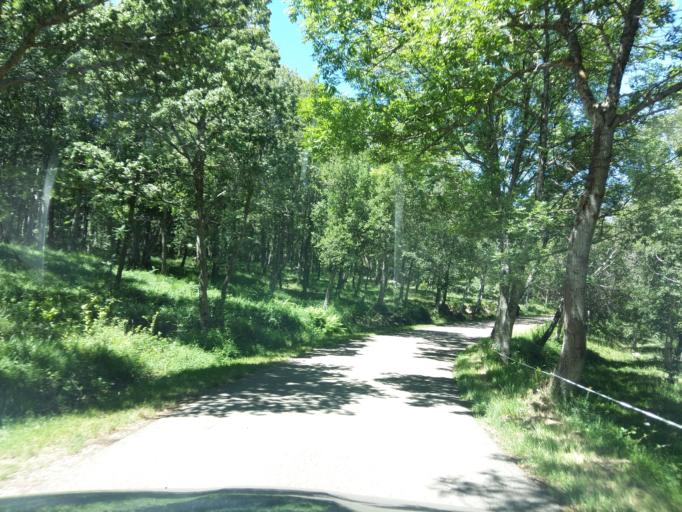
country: ES
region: Castille and Leon
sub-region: Provincia de Soria
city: Vozmediano
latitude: 41.8144
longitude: -1.8203
